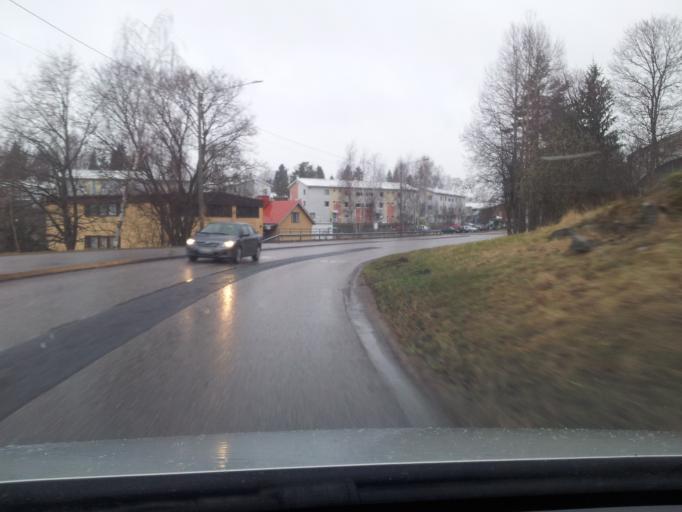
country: FI
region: Uusimaa
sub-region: Helsinki
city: Espoo
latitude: 60.1949
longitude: 24.5914
